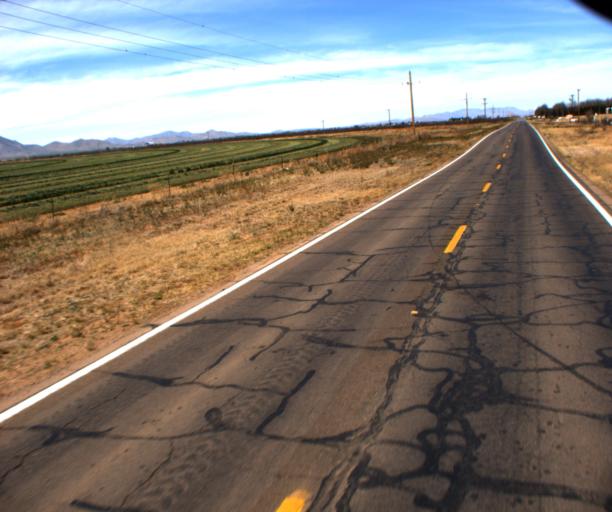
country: US
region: Arizona
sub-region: Cochise County
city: Willcox
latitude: 31.9609
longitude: -109.8413
